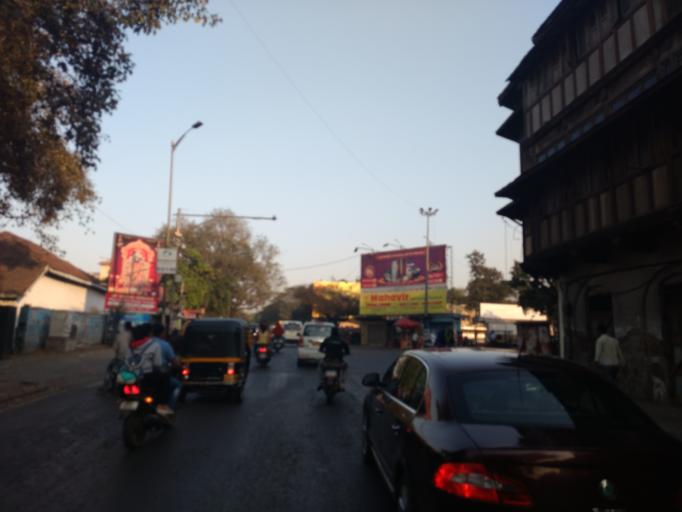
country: IN
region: Maharashtra
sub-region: Pune Division
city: Pune
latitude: 18.5066
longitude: 73.8815
